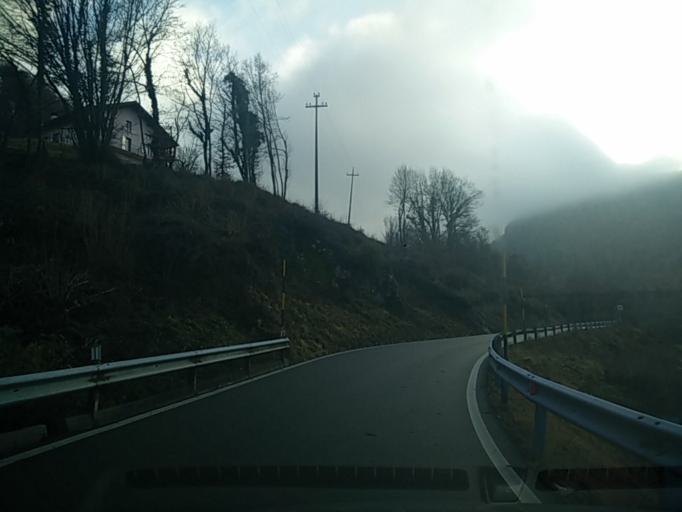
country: IT
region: Veneto
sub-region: Provincia di Belluno
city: Trichiana
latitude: 46.0263
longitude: 12.1627
